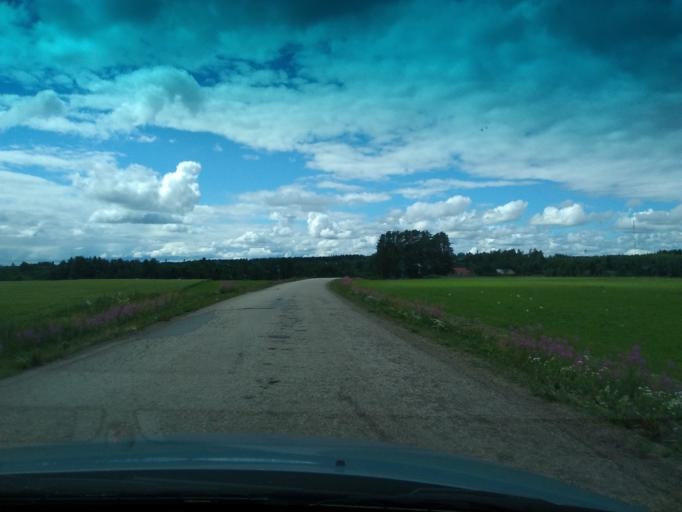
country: FI
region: Central Finland
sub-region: Saarijaervi-Viitasaari
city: Saarijaervi
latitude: 62.8121
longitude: 25.0336
